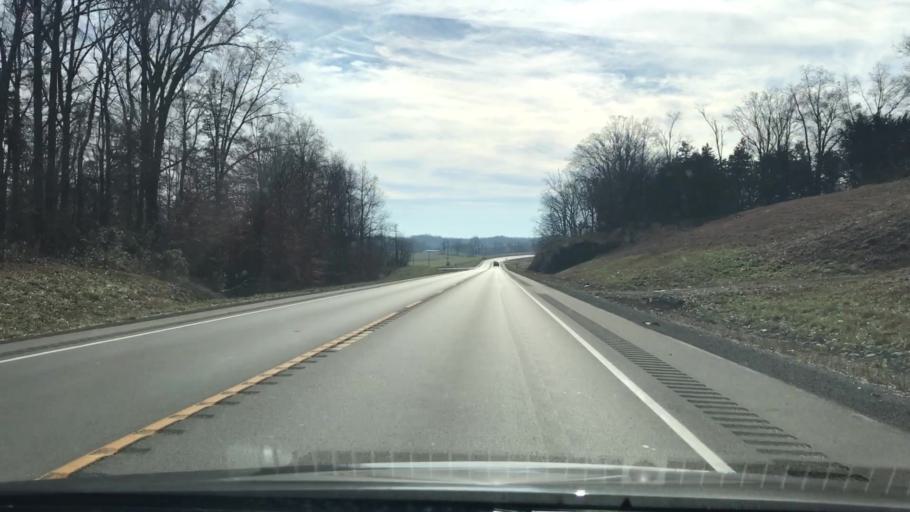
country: US
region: Kentucky
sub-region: Monroe County
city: Tompkinsville
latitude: 36.7653
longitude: -85.6859
